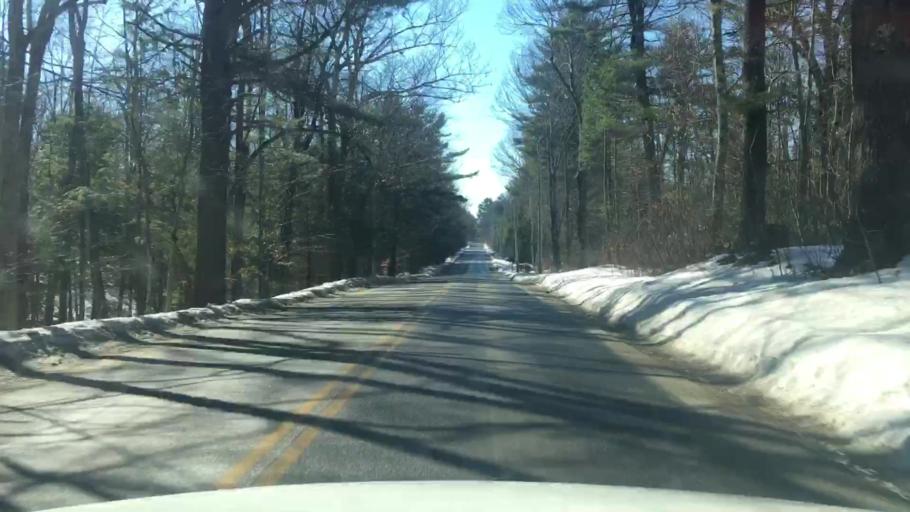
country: US
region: Maine
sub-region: Cumberland County
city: North Windham
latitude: 43.8468
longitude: -70.3548
